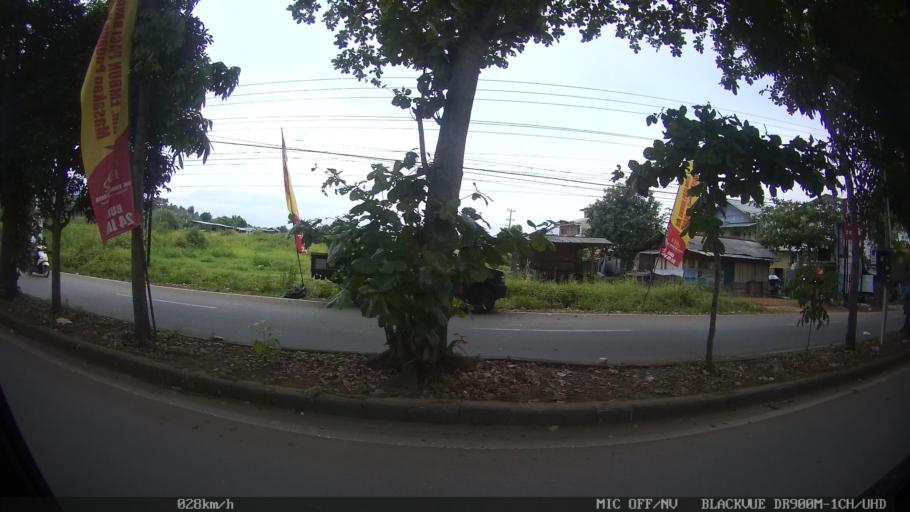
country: ID
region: Lampung
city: Kedaton
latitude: -5.3989
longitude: 105.2035
